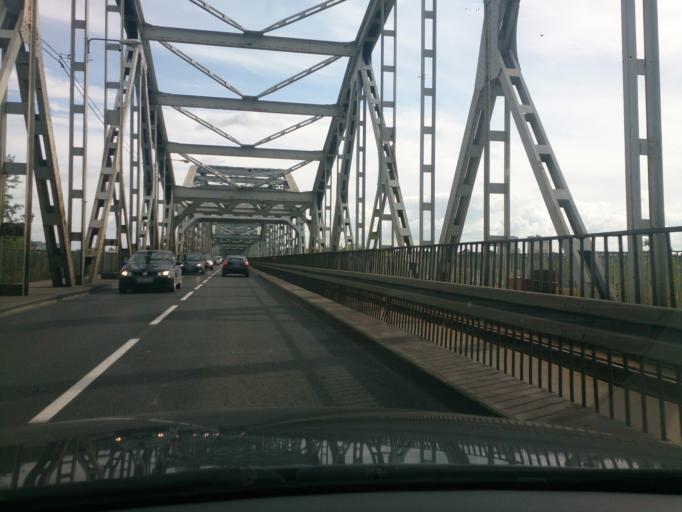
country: PL
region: Kujawsko-Pomorskie
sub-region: Grudziadz
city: Grudziadz
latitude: 53.4856
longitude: 18.7338
